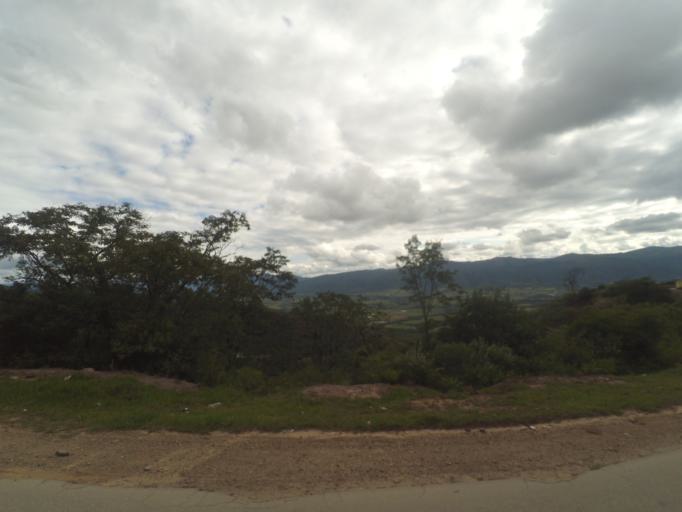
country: BO
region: Santa Cruz
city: Samaipata
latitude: -18.1729
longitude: -63.8786
